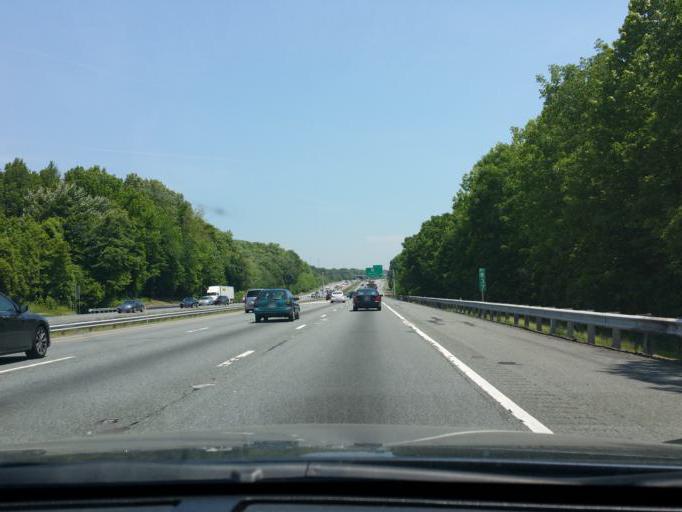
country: US
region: Maryland
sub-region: Harford County
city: Aberdeen
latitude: 39.5165
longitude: -76.2030
